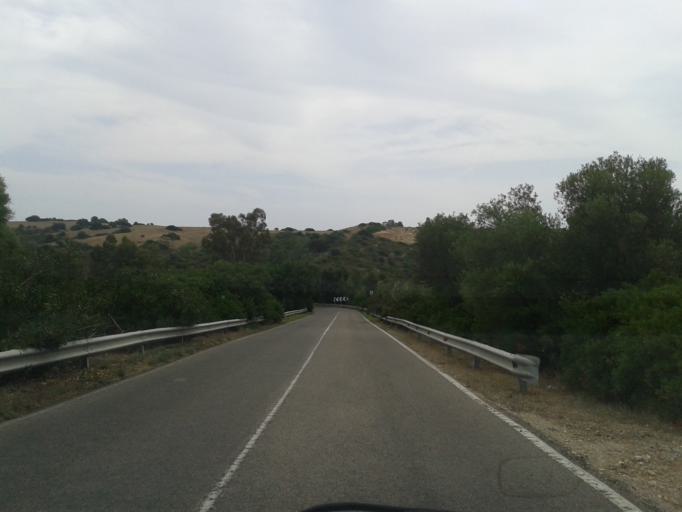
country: IT
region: Sardinia
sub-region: Provincia di Cagliari
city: Olia Speciosa
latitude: 39.2836
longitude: 9.5665
